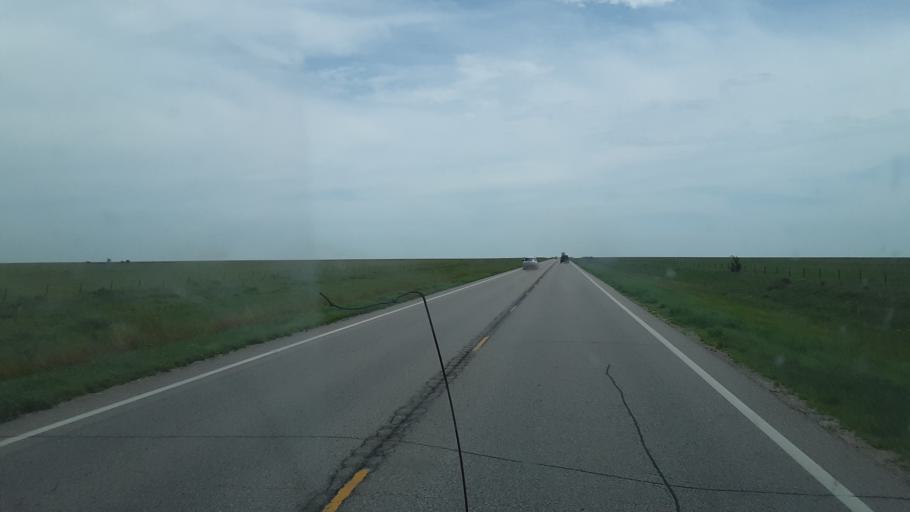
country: US
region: Kansas
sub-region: Butler County
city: El Dorado
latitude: 37.8102
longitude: -96.5907
